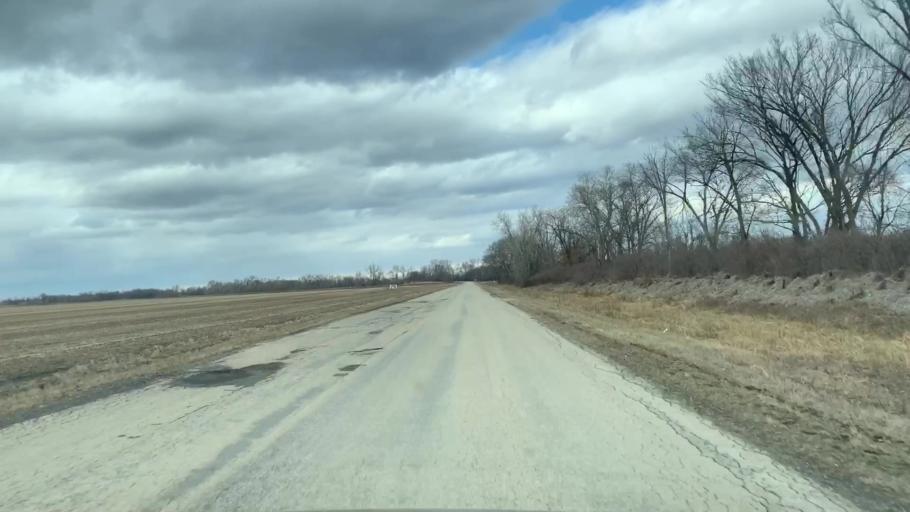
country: US
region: Kansas
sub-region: Allen County
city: Humboldt
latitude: 37.7955
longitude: -95.4706
